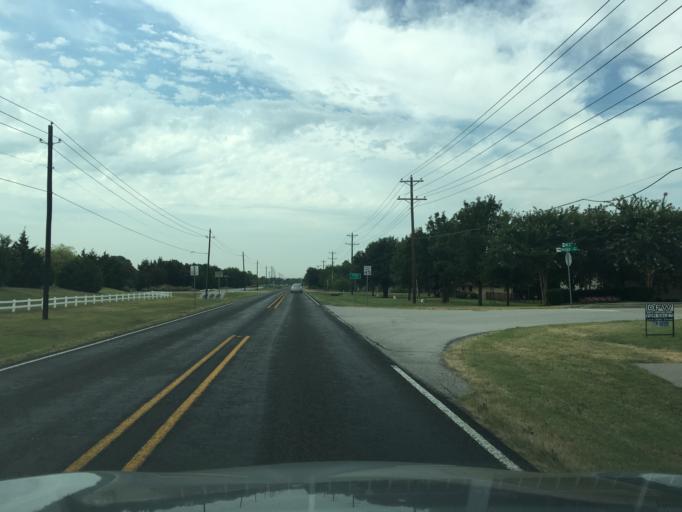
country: US
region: Texas
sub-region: Collin County
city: Parker
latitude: 33.0743
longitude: -96.6203
